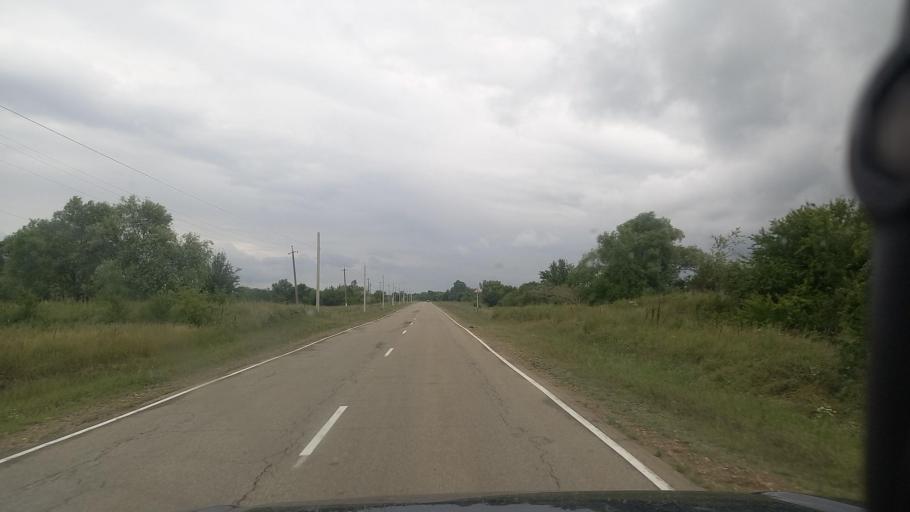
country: RU
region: Adygeya
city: Adygeysk
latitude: 44.8847
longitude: 39.2465
